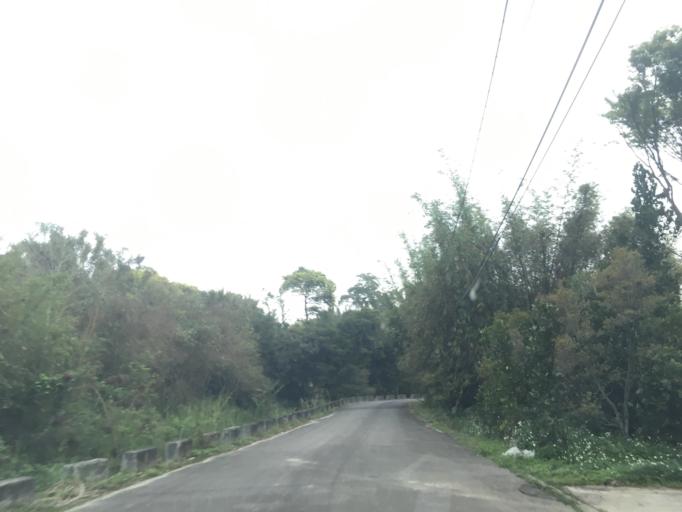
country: TW
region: Taiwan
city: Daxi
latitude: 24.8786
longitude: 121.3081
